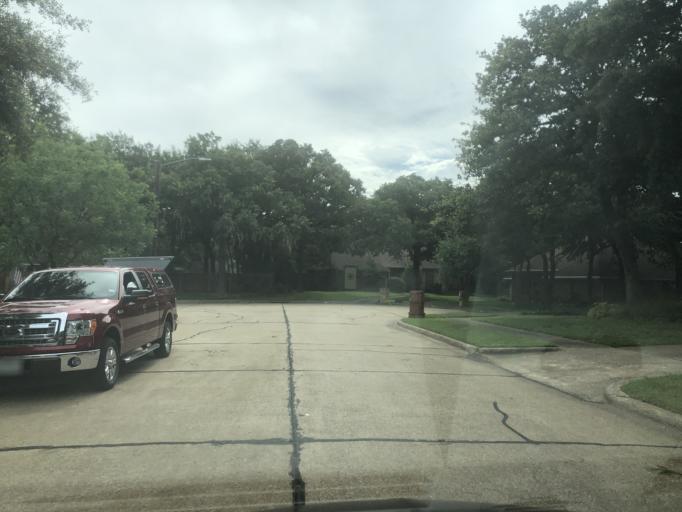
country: US
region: Texas
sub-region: Dallas County
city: Irving
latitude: 32.7975
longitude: -96.9838
